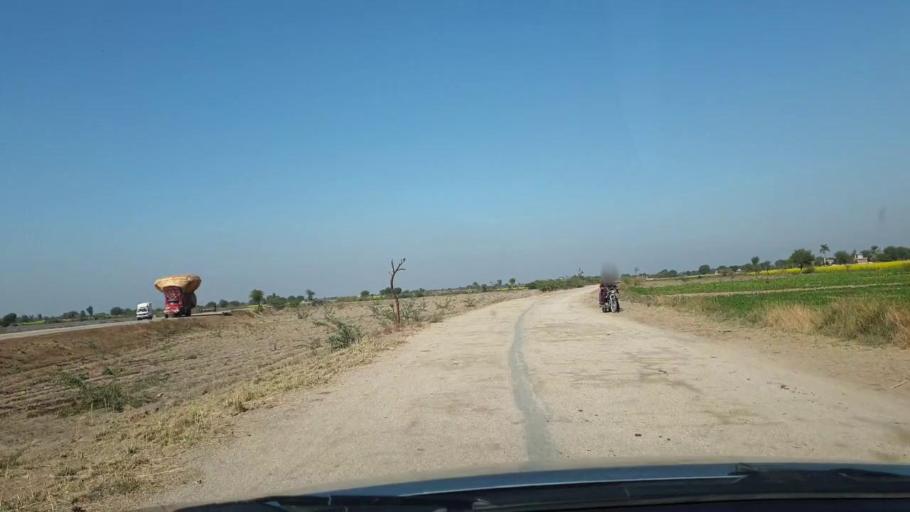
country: PK
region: Sindh
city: Jhol
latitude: 25.9215
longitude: 68.9081
